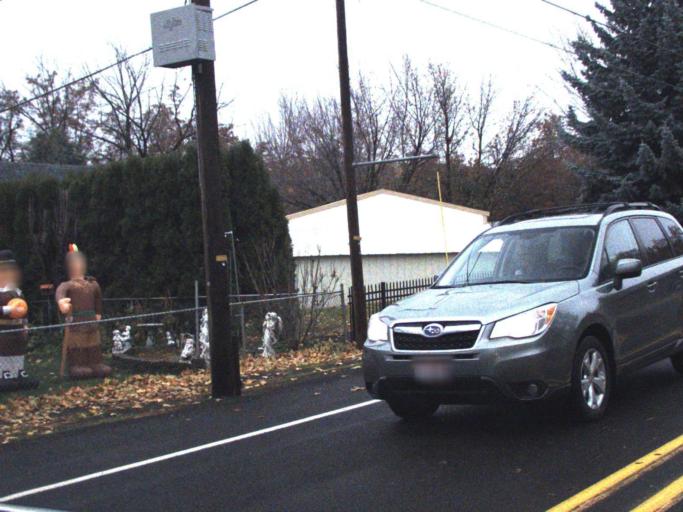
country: US
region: Washington
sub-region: Walla Walla County
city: Waitsburg
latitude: 46.1409
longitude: -118.1533
